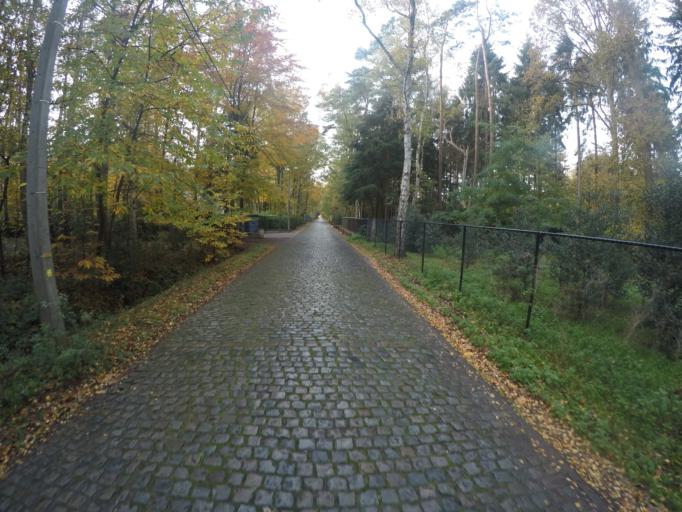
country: BE
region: Flanders
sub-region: Provincie Oost-Vlaanderen
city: Temse
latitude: 51.1707
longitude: 4.2038
